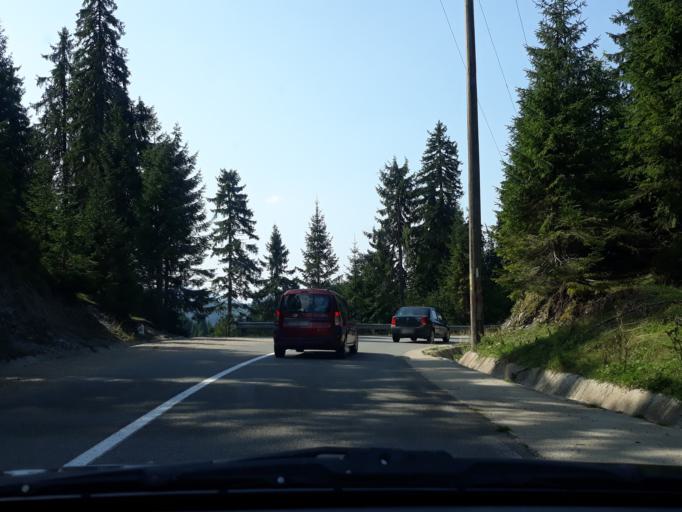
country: RO
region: Alba
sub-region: Comuna Arieseni
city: Arieseni
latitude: 46.5927
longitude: 22.7034
